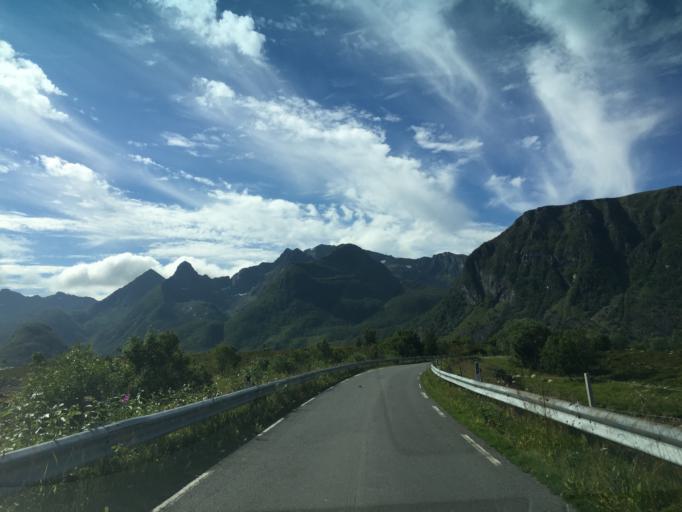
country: NO
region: Nordland
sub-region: Vagan
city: Svolvaer
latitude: 68.3954
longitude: 14.5621
